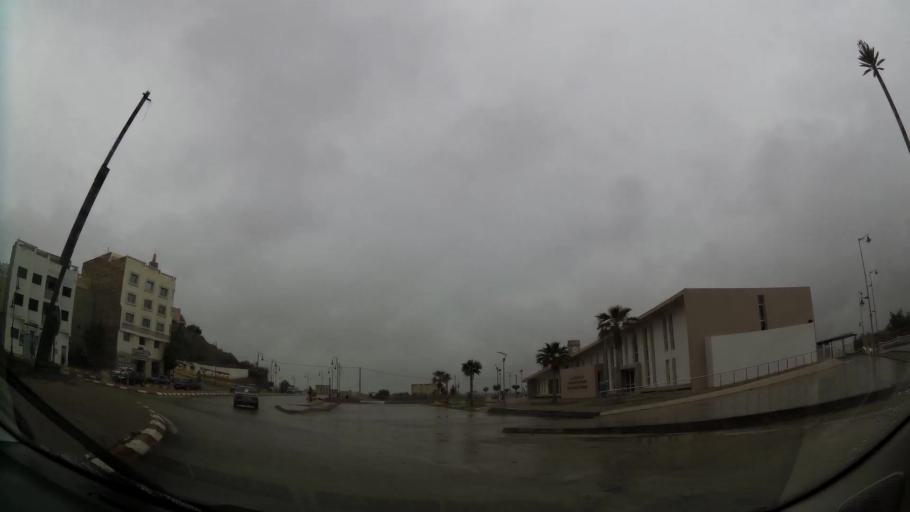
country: MA
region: Taza-Al Hoceima-Taounate
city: Imzourene
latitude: 35.1560
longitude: -3.8491
